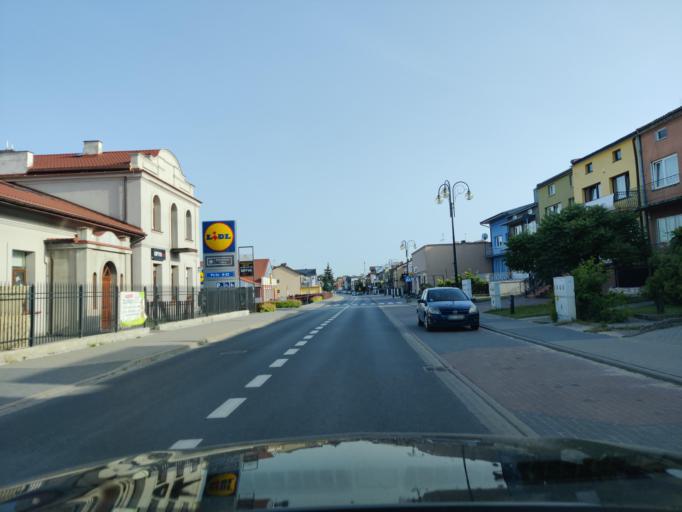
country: PL
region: Masovian Voivodeship
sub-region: Powiat wyszkowski
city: Wyszkow
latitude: 52.5991
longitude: 21.4564
